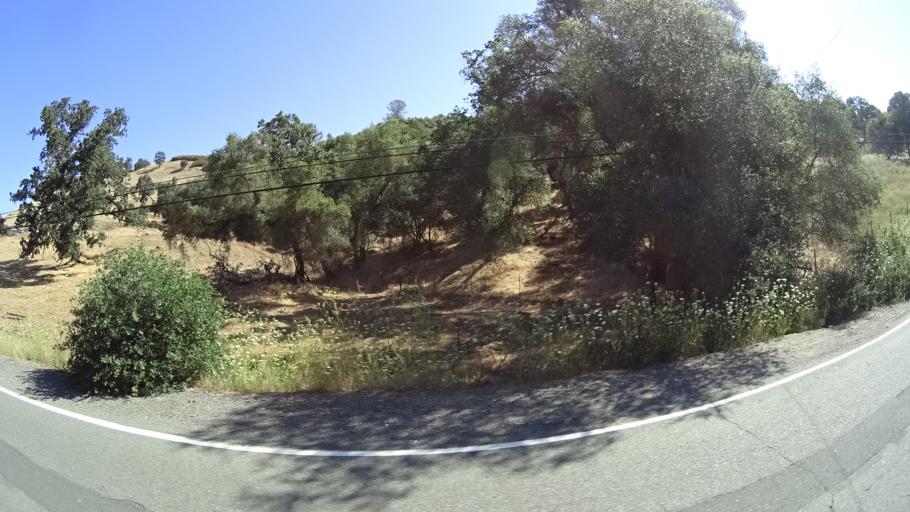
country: US
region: California
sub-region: Calaveras County
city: San Andreas
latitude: 38.2123
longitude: -120.6859
